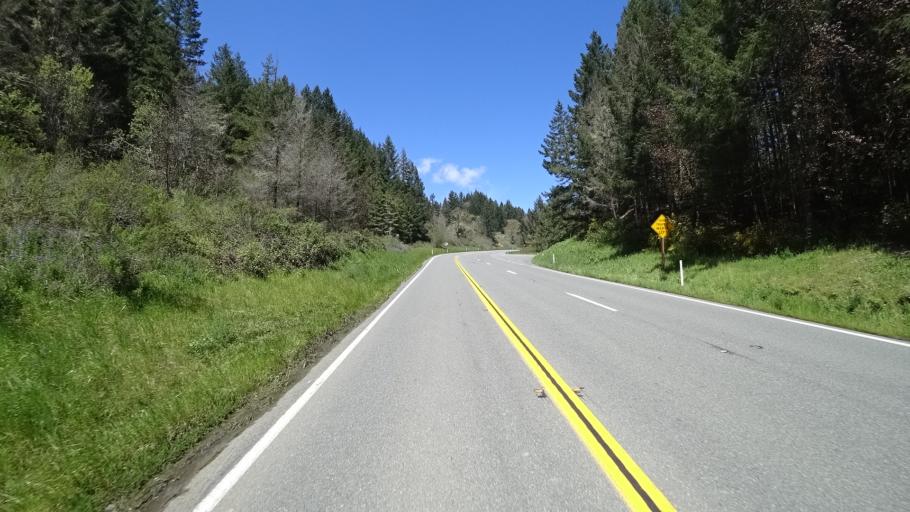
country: US
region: California
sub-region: Humboldt County
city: Blue Lake
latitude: 40.9117
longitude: -123.8250
